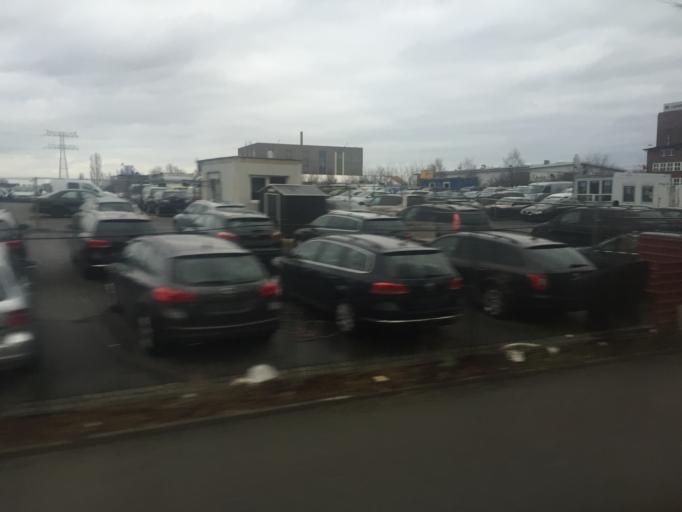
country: DE
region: Berlin
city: Baumschulenweg
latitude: 52.4646
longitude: 13.4982
